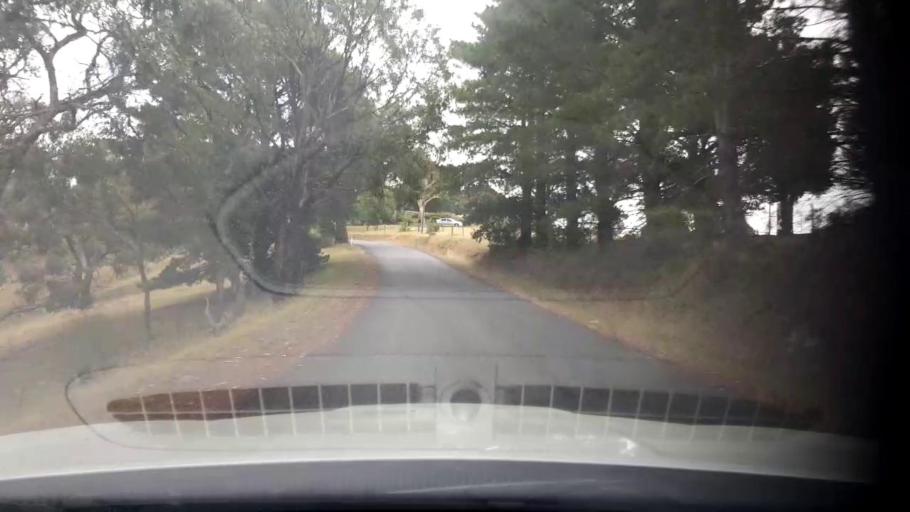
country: AU
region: Victoria
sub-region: Whittlesea
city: Whittlesea
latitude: -37.4895
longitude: 145.0560
